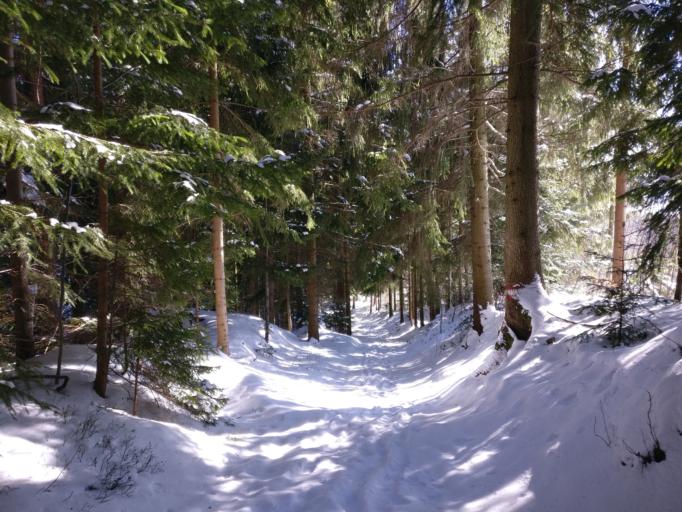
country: AT
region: Styria
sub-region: Politischer Bezirk Hartberg-Fuerstenfeld
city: Sankt Jakob im Walde
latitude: 47.4726
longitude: 15.7872
